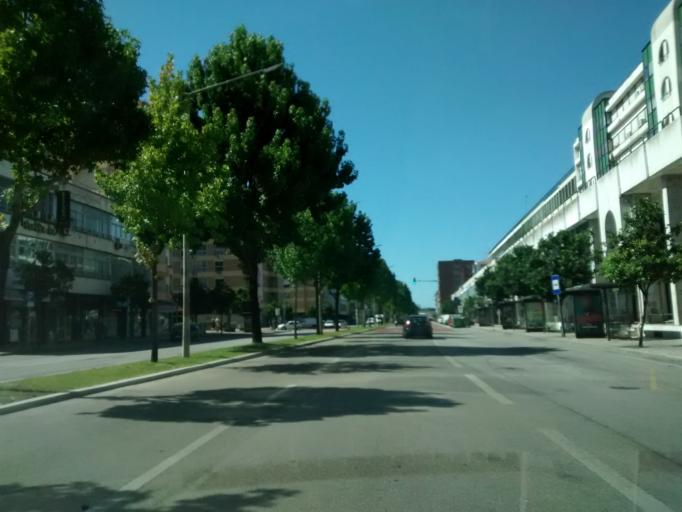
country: PT
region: Coimbra
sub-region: Coimbra
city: Coimbra
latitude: 40.2137
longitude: -8.4338
